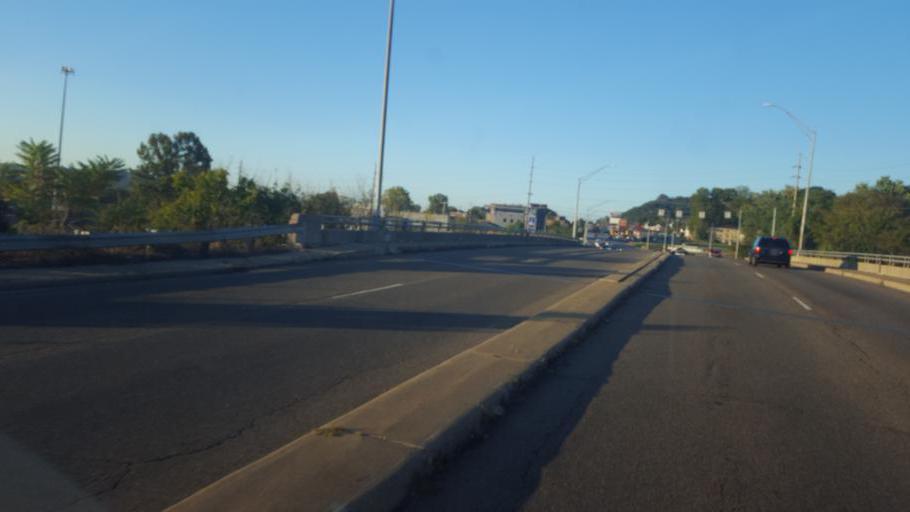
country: US
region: Ohio
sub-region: Scioto County
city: Portsmouth
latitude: 38.7455
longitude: -82.9927
